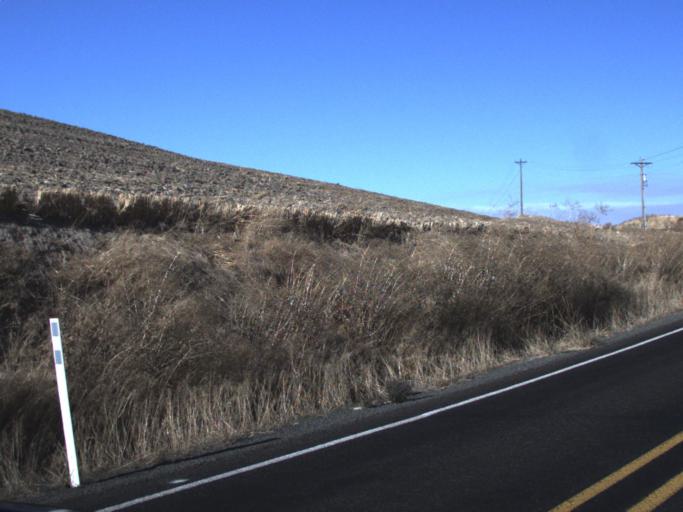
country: US
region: Washington
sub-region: Walla Walla County
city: Walla Walla
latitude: 46.1403
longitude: -118.3730
